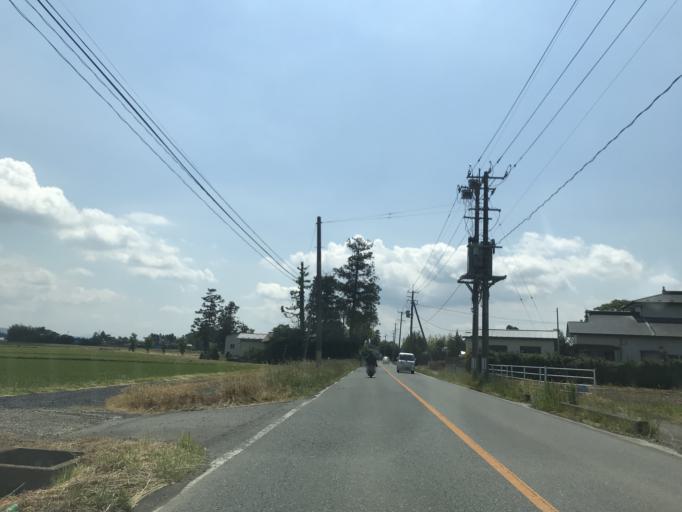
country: JP
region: Miyagi
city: Kogota
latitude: 38.5750
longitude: 141.0351
